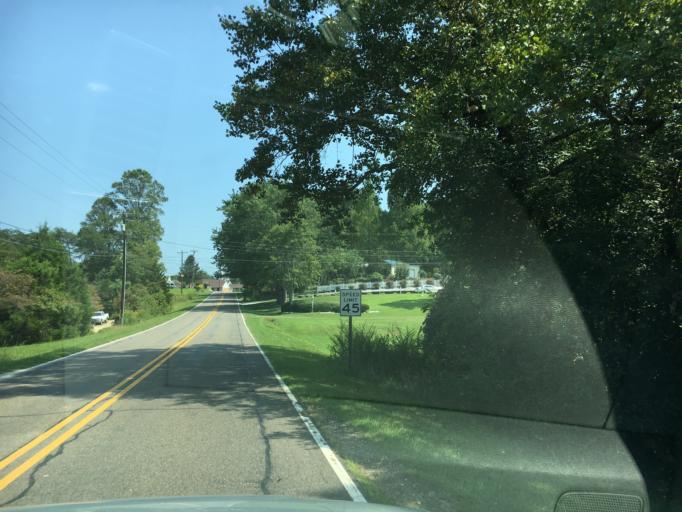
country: US
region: North Carolina
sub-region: McDowell County
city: Marion
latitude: 35.7102
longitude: -81.8995
